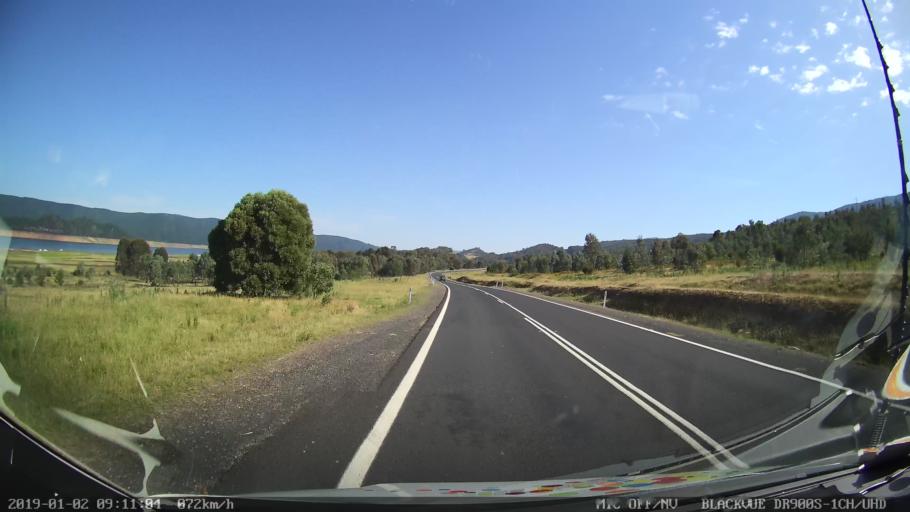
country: AU
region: New South Wales
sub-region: Tumut Shire
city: Tumut
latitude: -35.5152
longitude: 148.2688
